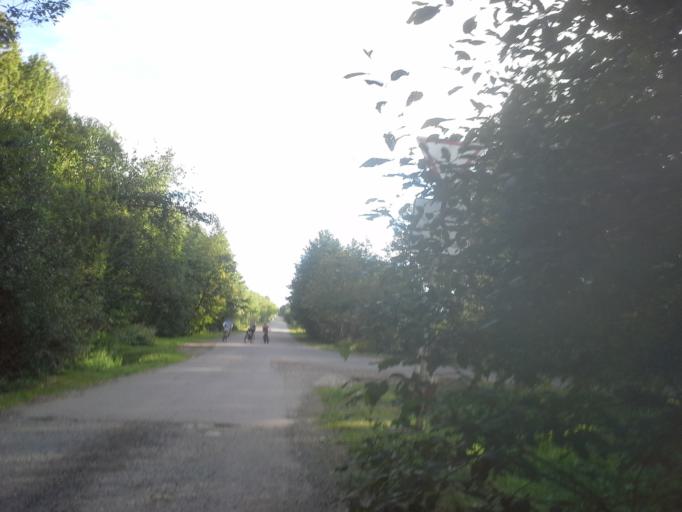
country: RU
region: Moskovskaya
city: Kievskij
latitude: 55.4325
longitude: 36.8281
